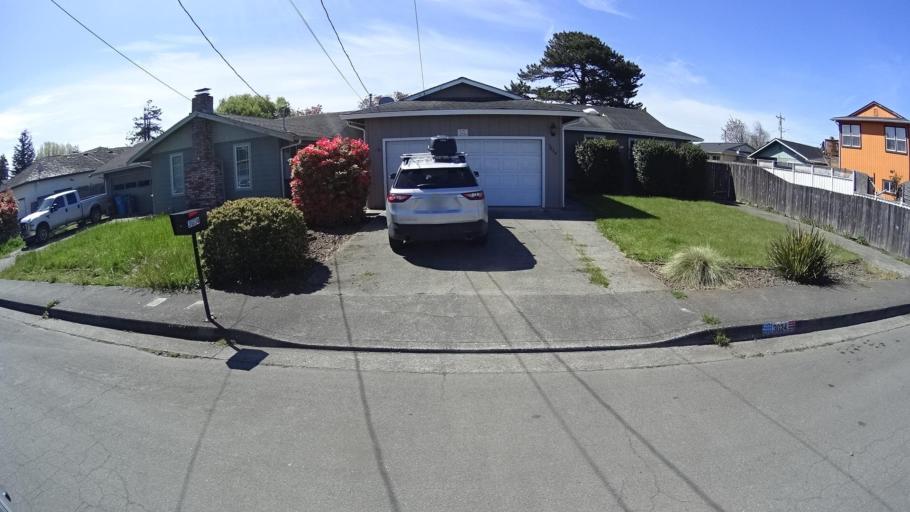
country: US
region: California
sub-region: Humboldt County
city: Myrtletown
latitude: 40.7865
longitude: -124.1278
